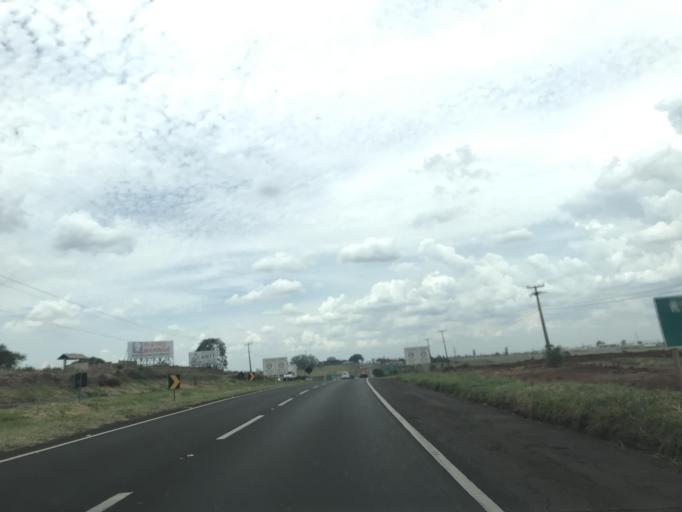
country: BR
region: Parana
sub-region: Paicandu
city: Paicandu
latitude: -23.3914
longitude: -52.0125
